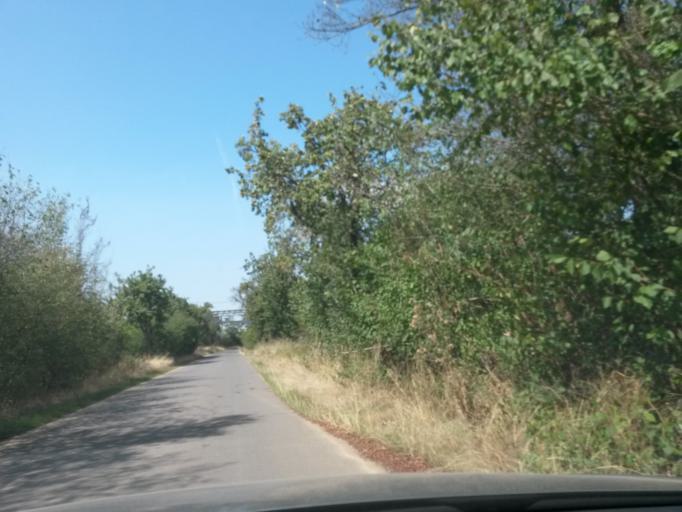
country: DE
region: Saxony-Anhalt
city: Jerichow
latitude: 52.3946
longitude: 11.9880
